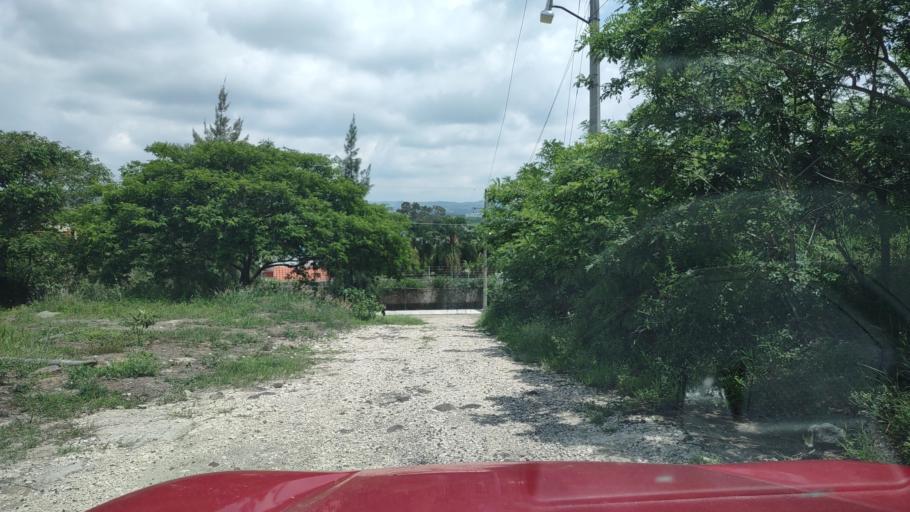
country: MX
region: Veracruz
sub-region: Emiliano Zapata
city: Dos Rios
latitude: 19.4624
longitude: -96.7892
